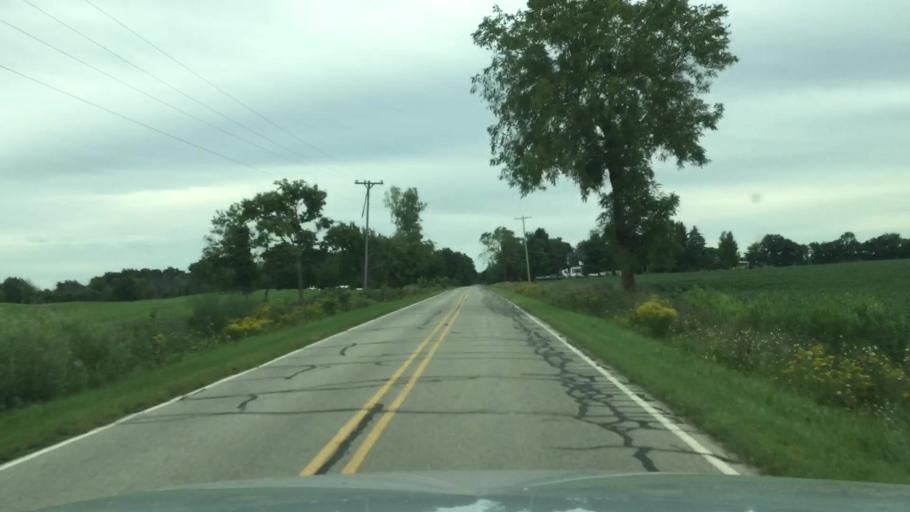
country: US
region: Michigan
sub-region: Shiawassee County
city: Corunna
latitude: 42.9264
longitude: -84.0770
